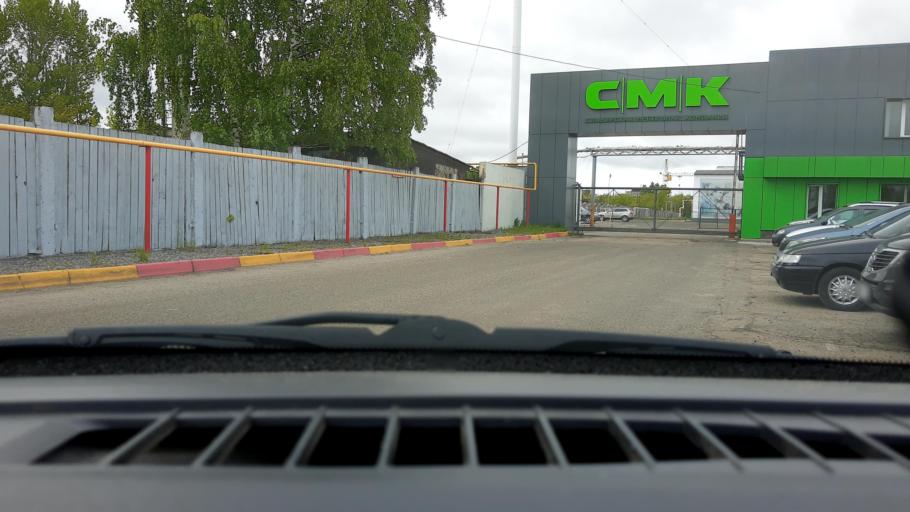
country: RU
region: Nizjnij Novgorod
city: Gorbatovka
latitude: 56.3516
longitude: 43.8223
